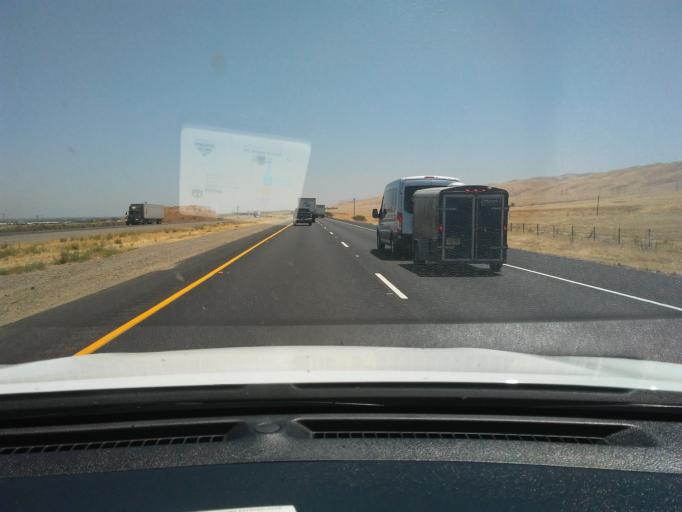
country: US
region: California
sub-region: San Joaquin County
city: Tracy
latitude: 37.6048
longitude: -121.3518
